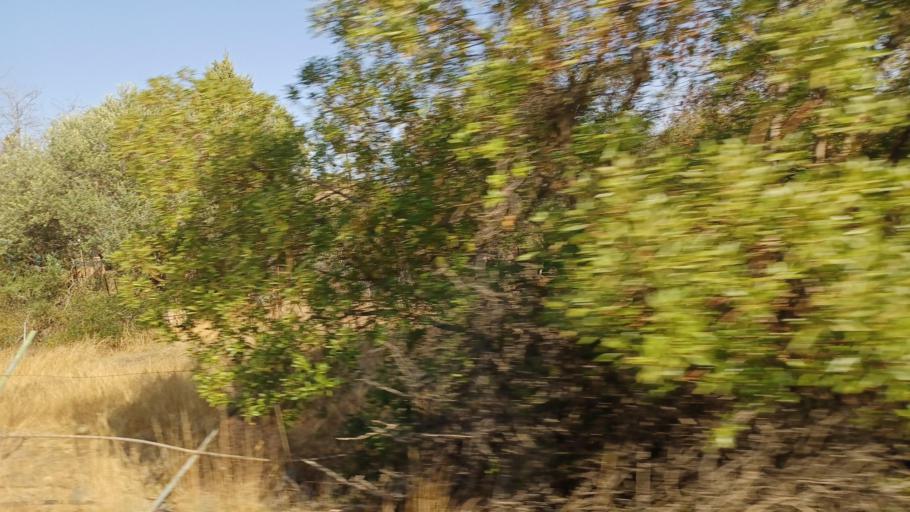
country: CY
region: Lefkosia
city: Alampra
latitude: 34.9829
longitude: 33.3534
